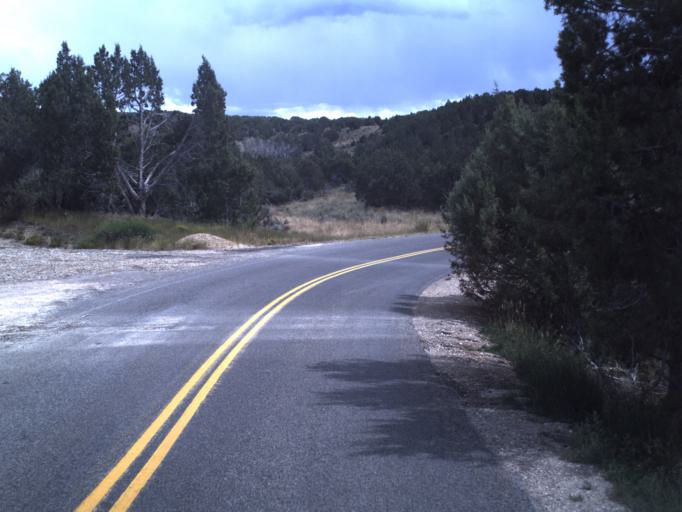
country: US
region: Utah
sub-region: Summit County
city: Oakley
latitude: 40.7816
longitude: -111.3916
